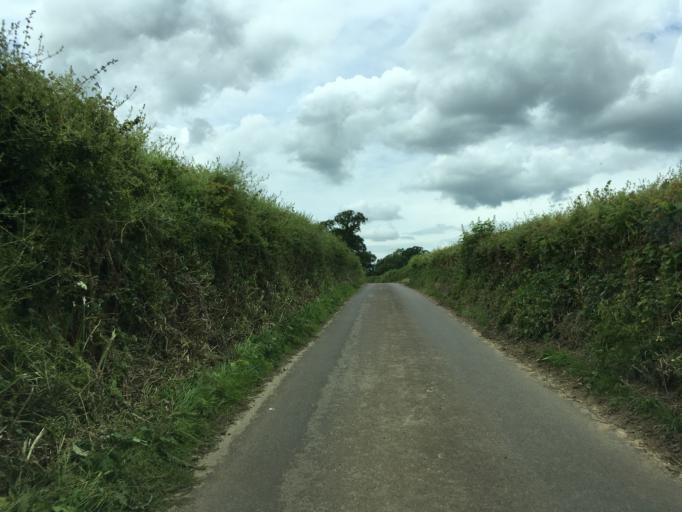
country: GB
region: England
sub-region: Wiltshire
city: Nettleton
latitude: 51.5157
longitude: -2.2319
